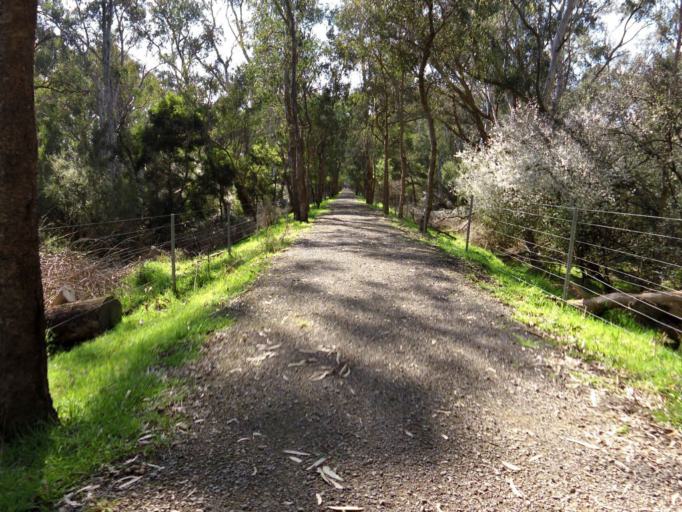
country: AU
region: Victoria
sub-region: Murrindindi
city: Alexandra
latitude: -37.1589
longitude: 145.5673
